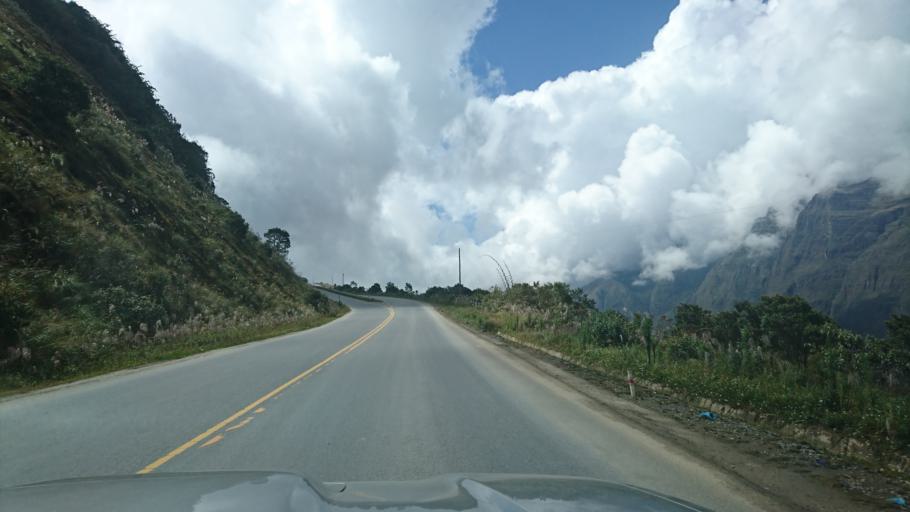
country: BO
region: La Paz
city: Coroico
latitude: -16.2888
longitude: -67.8797
